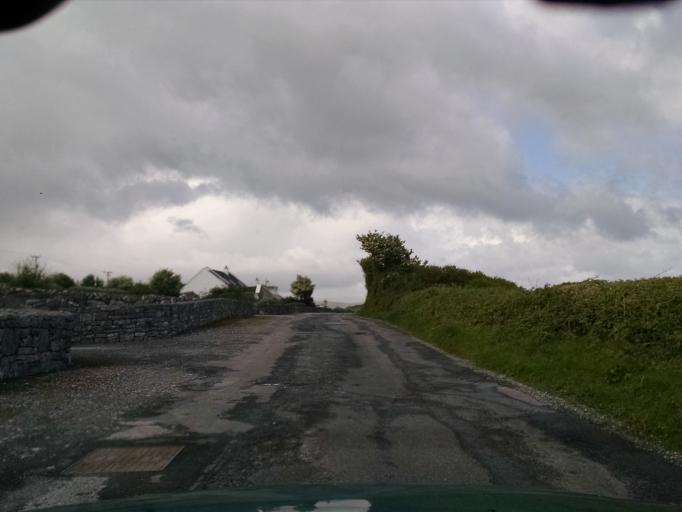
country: IE
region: Connaught
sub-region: County Galway
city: Gaillimh
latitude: 53.1561
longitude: -9.0663
